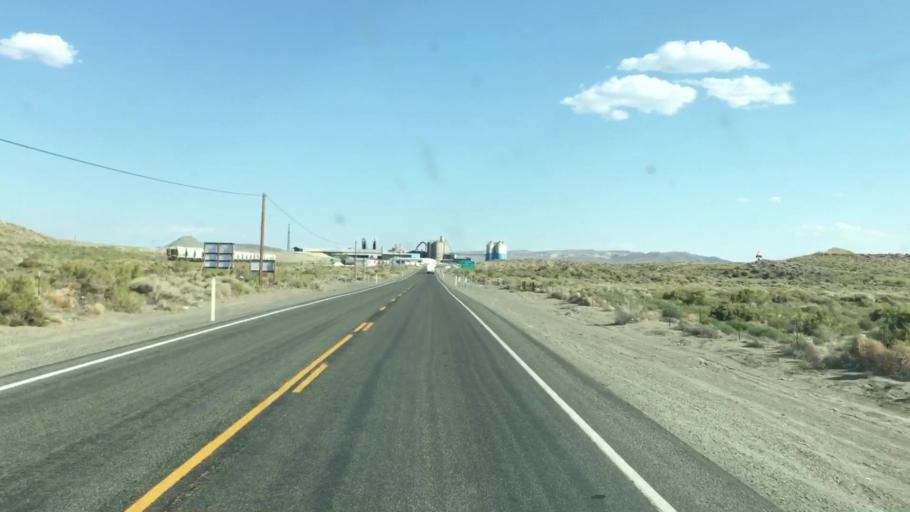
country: US
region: Nevada
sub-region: Lyon County
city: Fernley
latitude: 39.6278
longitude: -119.2739
